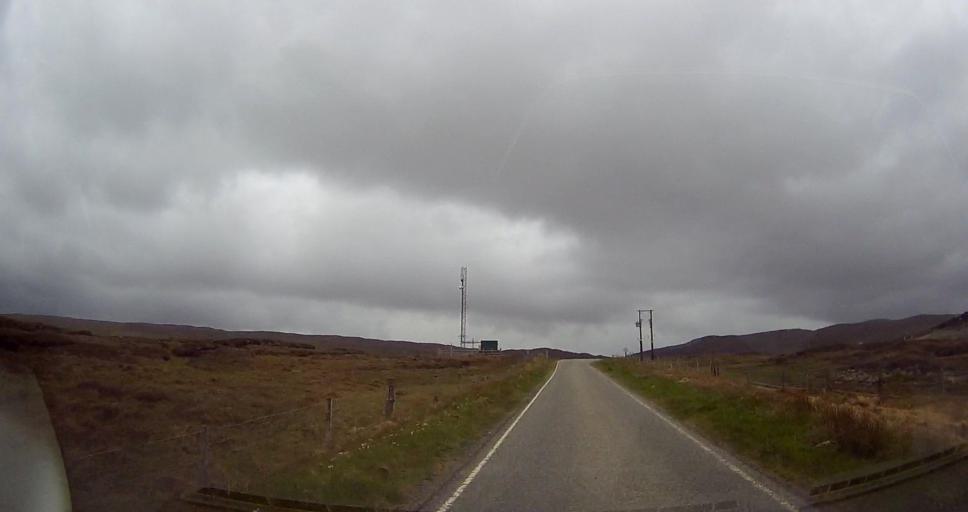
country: GB
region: Scotland
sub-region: Shetland Islands
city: Lerwick
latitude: 60.2768
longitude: -1.2615
